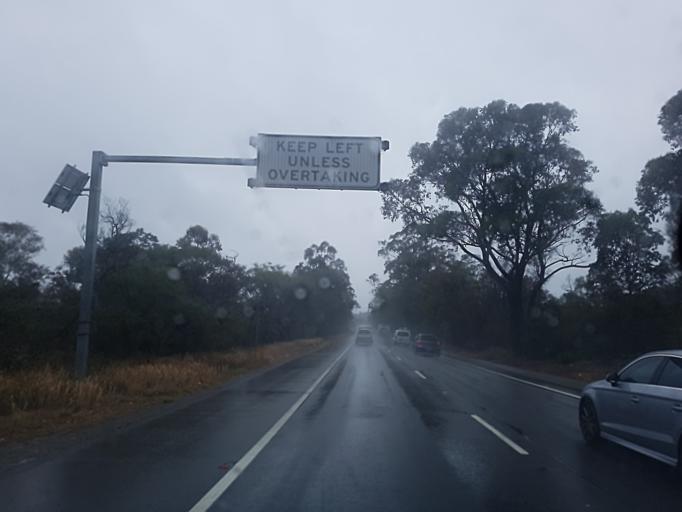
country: AU
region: New South Wales
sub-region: Warringah
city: Davidson
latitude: -33.7095
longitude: 151.1949
